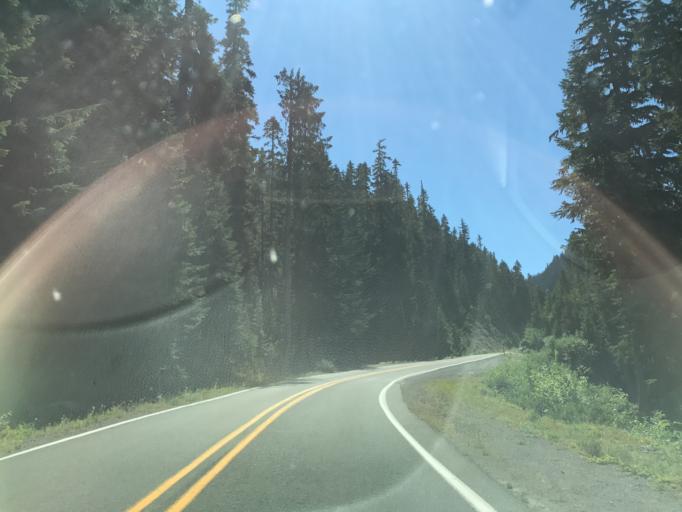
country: US
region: Washington
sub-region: King County
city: Enumclaw
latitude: 46.8793
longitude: -121.5391
